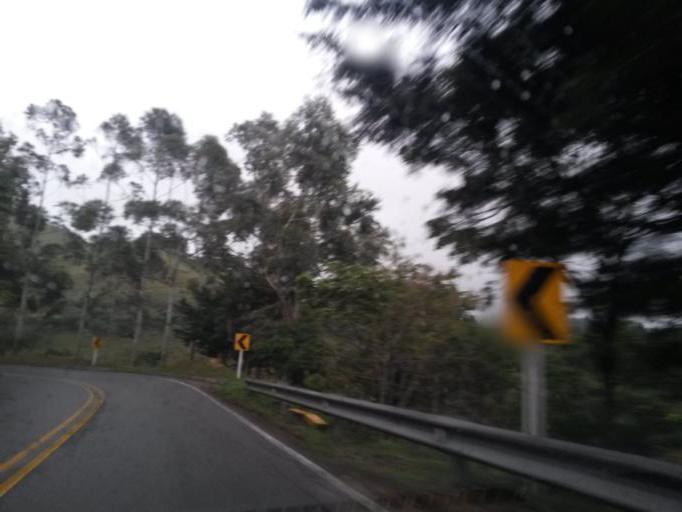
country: CO
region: Cauca
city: Popayan
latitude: 2.4068
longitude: -76.5040
